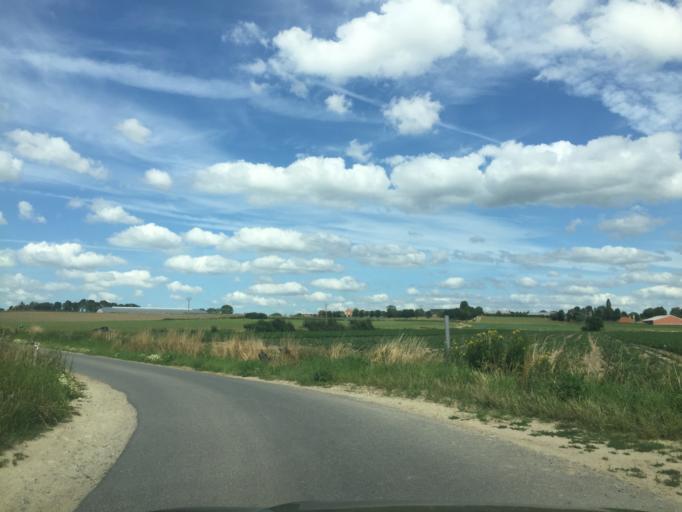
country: BE
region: Flanders
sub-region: Provincie West-Vlaanderen
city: Hooglede
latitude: 50.9788
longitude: 3.0567
